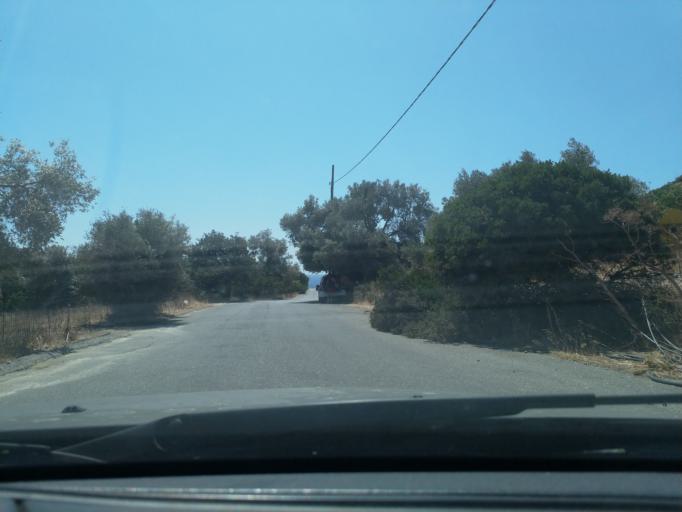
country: GR
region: Crete
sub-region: Nomos Rethymnis
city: Agia Galini
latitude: 35.1232
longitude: 24.5557
